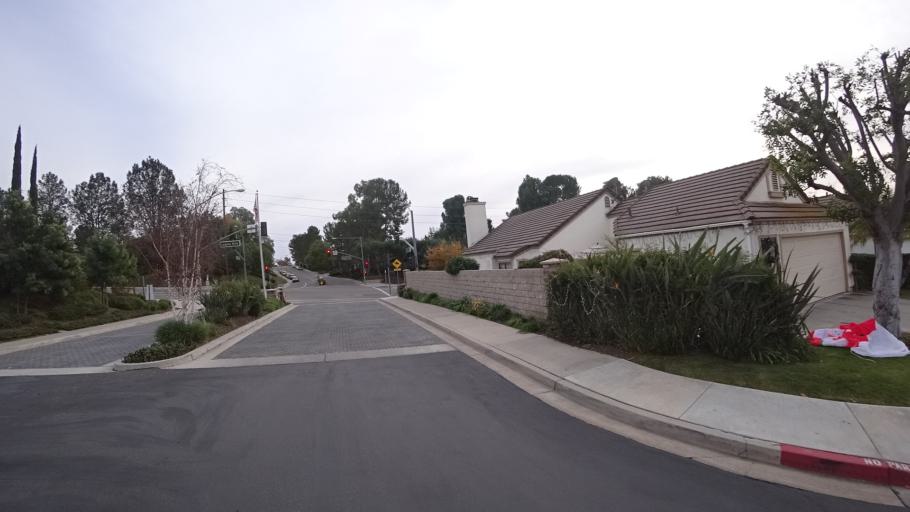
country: US
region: California
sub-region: Orange County
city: Laguna Hills
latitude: 33.5929
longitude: -117.7093
